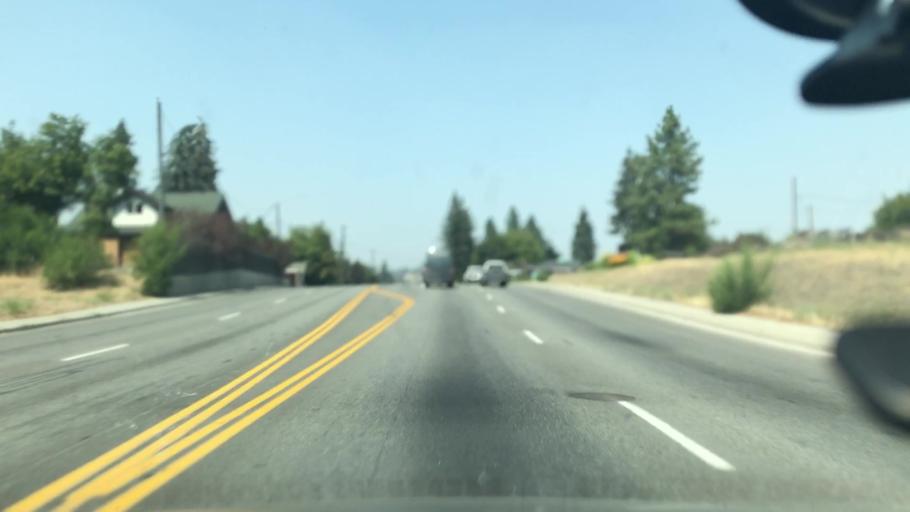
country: US
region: Washington
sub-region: Spokane County
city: Millwood
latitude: 47.6905
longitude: -117.2827
